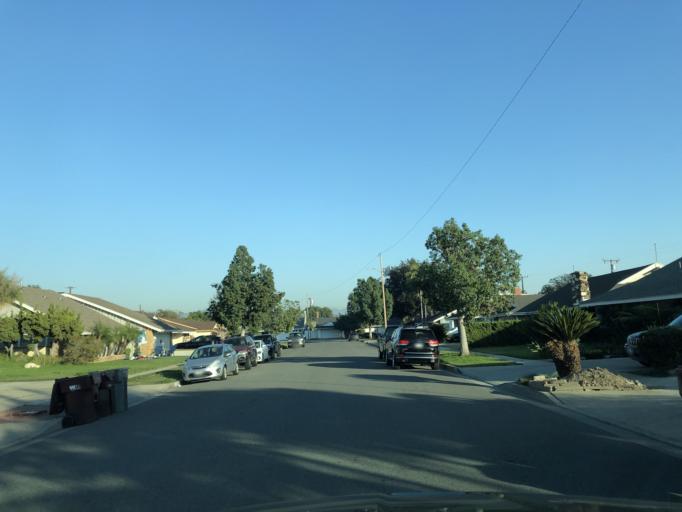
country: US
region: California
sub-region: Orange County
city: Orange
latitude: 33.7632
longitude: -117.8462
